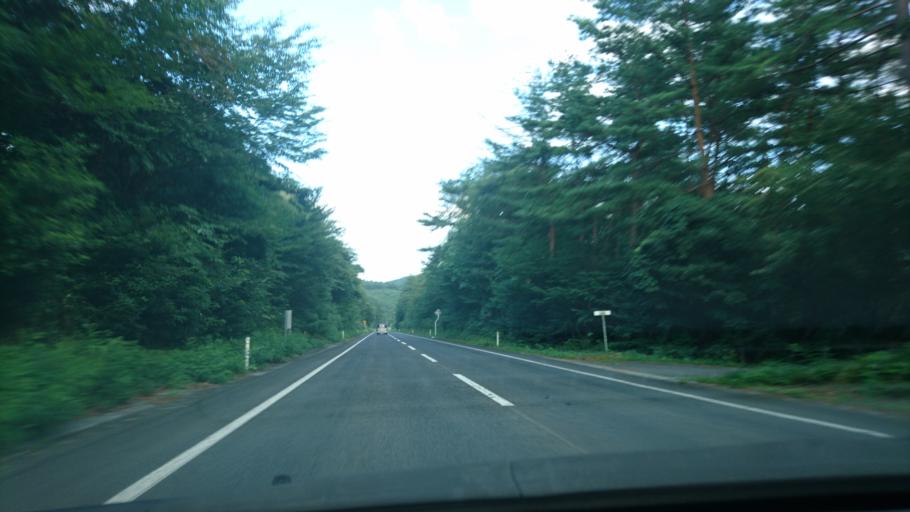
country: JP
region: Iwate
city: Mizusawa
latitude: 39.0308
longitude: 141.2774
